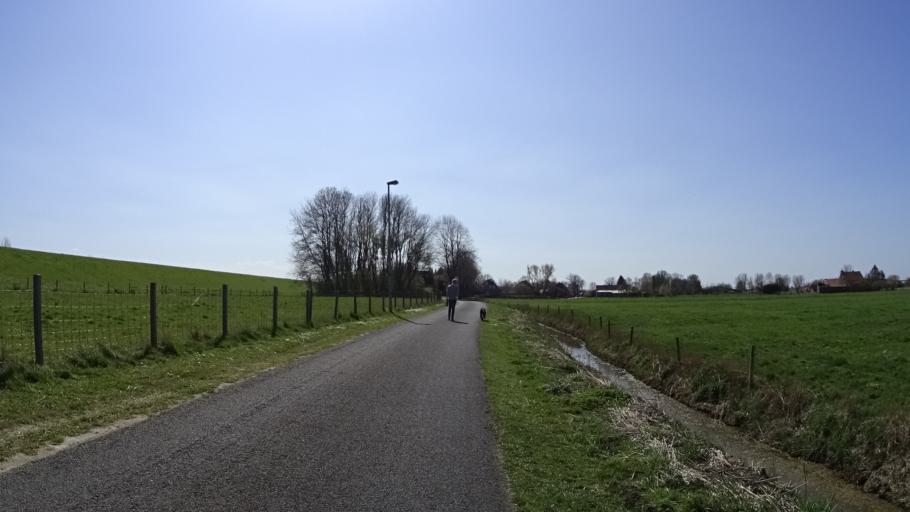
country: DE
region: Lower Saxony
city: Leer
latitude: 53.2053
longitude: 7.4041
